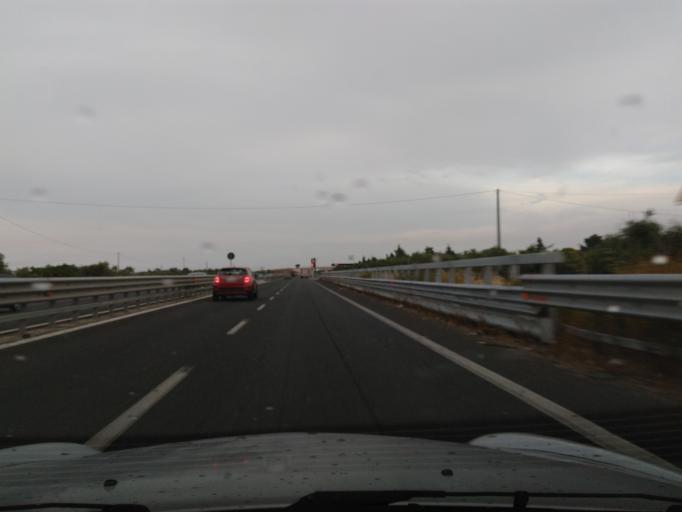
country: IT
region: Apulia
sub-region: Provincia di Bari
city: Giovinazzo
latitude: 41.1736
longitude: 16.6819
